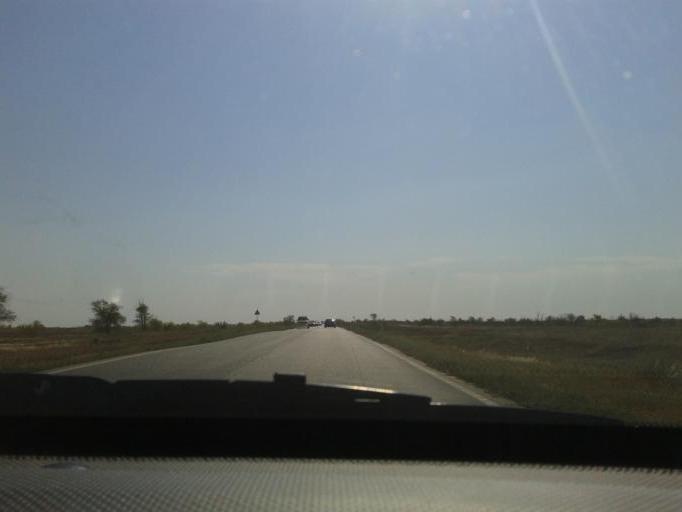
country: RU
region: Astrakhan
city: Znamensk
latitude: 48.6144
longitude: 45.5639
